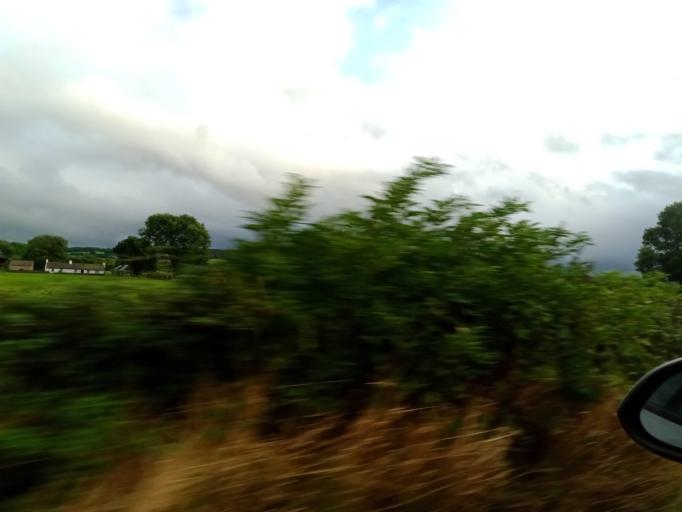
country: IE
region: Leinster
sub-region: Uibh Fhaili
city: Tullamore
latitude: 53.1441
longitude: -7.4689
